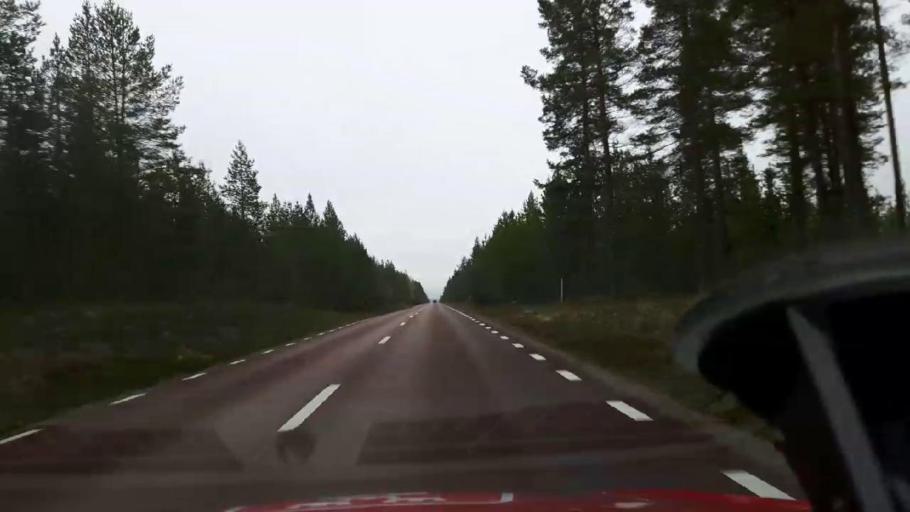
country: SE
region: Jaemtland
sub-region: Bergs Kommun
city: Hoverberg
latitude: 62.4468
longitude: 14.5675
